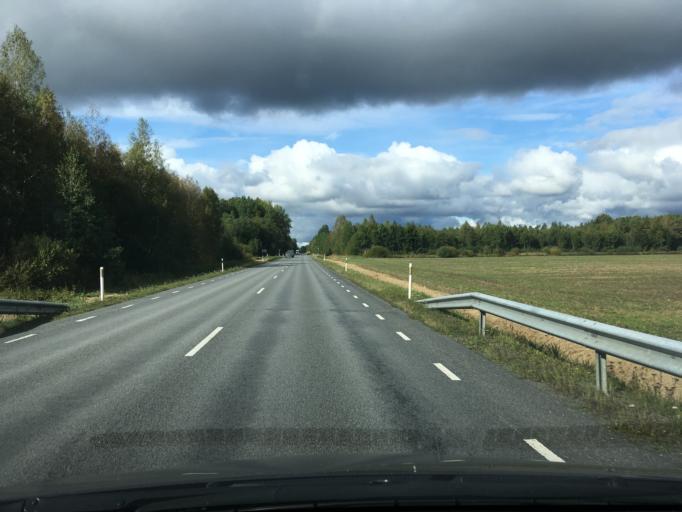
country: EE
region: Jaervamaa
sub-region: Tueri vald
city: Sarevere
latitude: 58.8042
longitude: 25.2195
